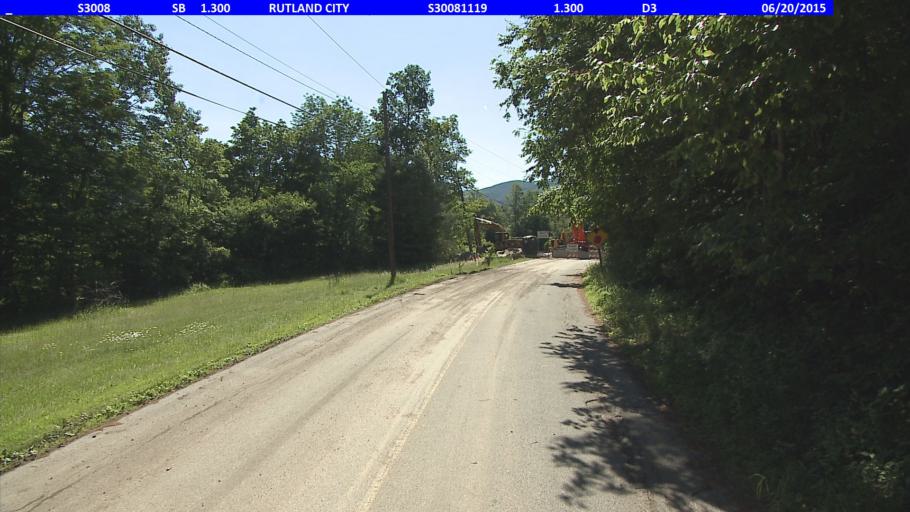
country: US
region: Vermont
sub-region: Rutland County
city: Rutland
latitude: 43.6021
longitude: -72.9945
